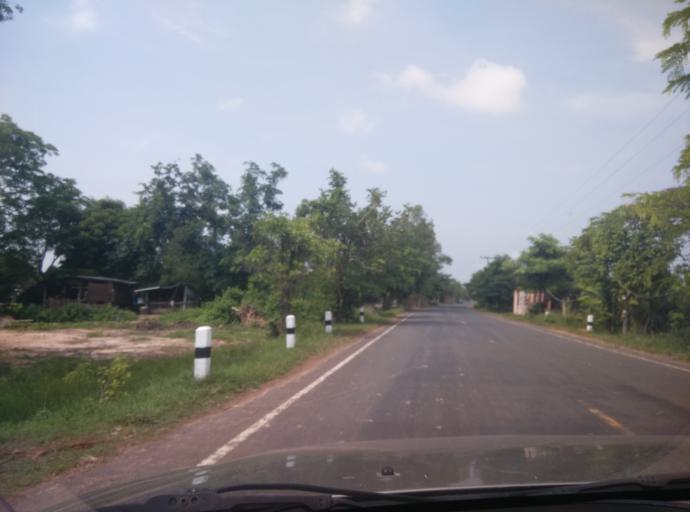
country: TH
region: Sisaket
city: Huai Thap Than
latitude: 15.0264
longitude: 104.0736
